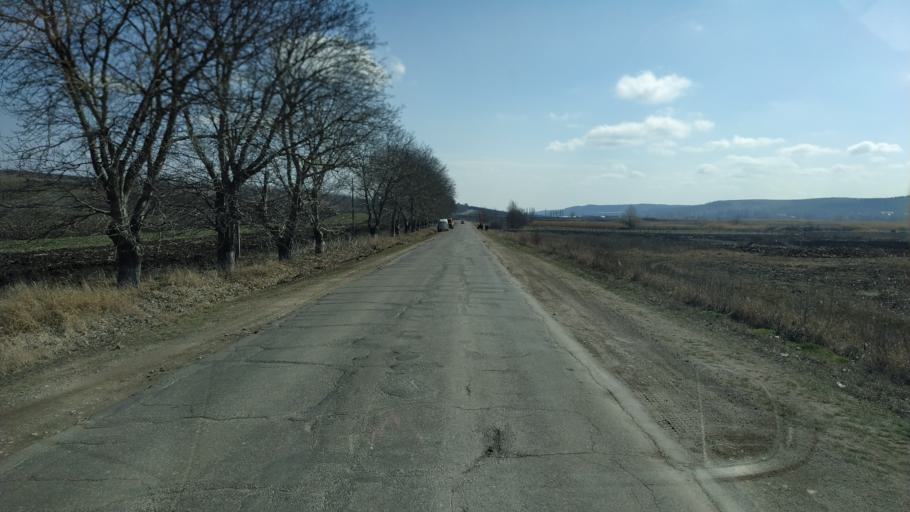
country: MD
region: Laloveni
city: Ialoveni
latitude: 46.9274
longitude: 28.6758
